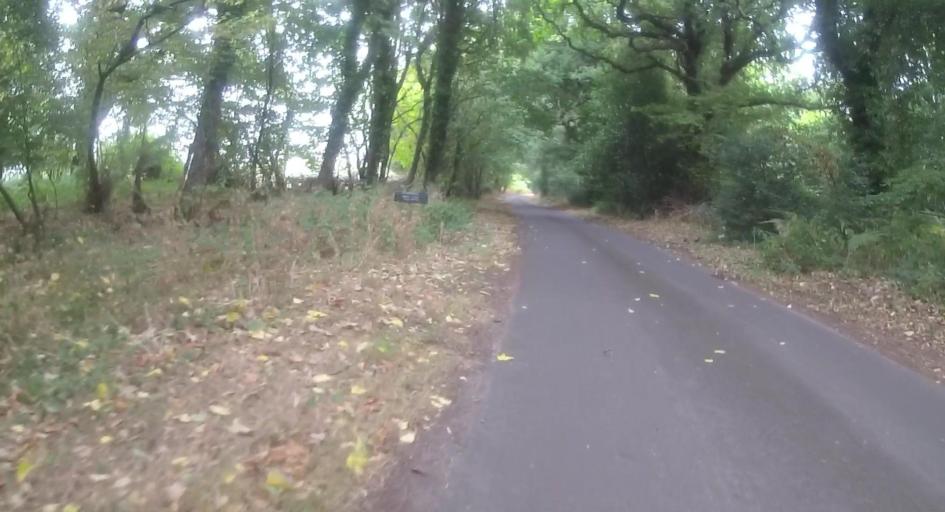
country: GB
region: England
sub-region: Dorset
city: Wool
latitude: 50.7190
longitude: -2.1898
